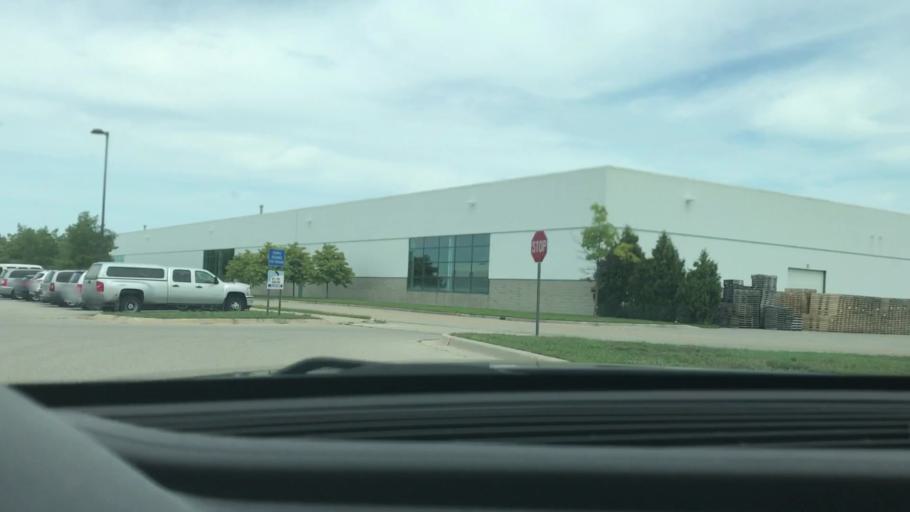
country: US
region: Michigan
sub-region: Charlevoix County
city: Charlevoix
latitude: 45.3023
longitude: -85.2648
